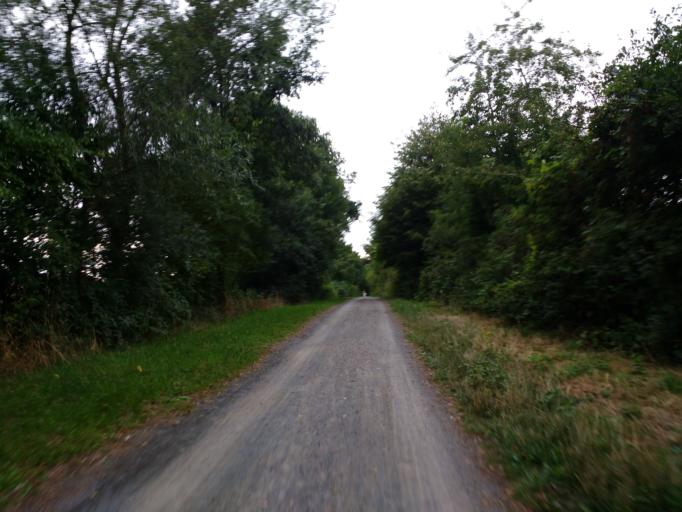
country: DE
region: Lower Saxony
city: Weyhausen
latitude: 52.4257
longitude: 10.6916
